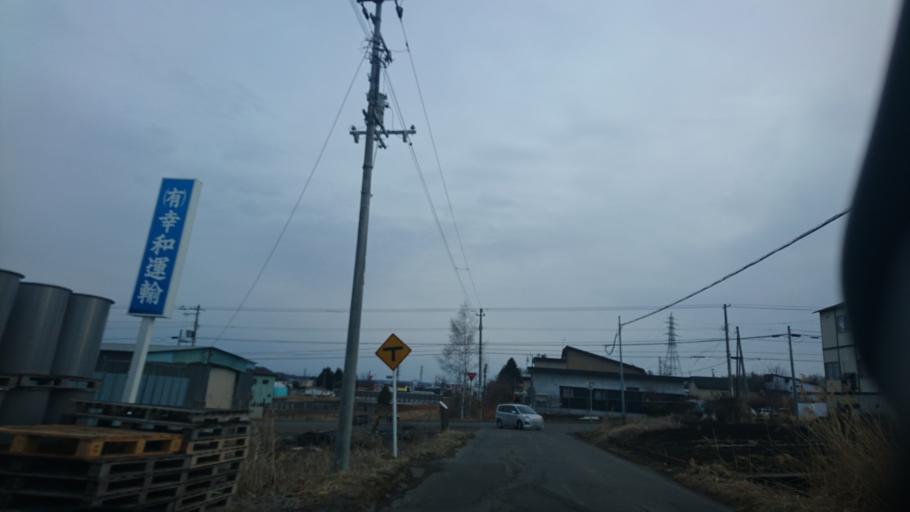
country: JP
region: Hokkaido
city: Otofuke
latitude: 42.9777
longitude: 143.2048
